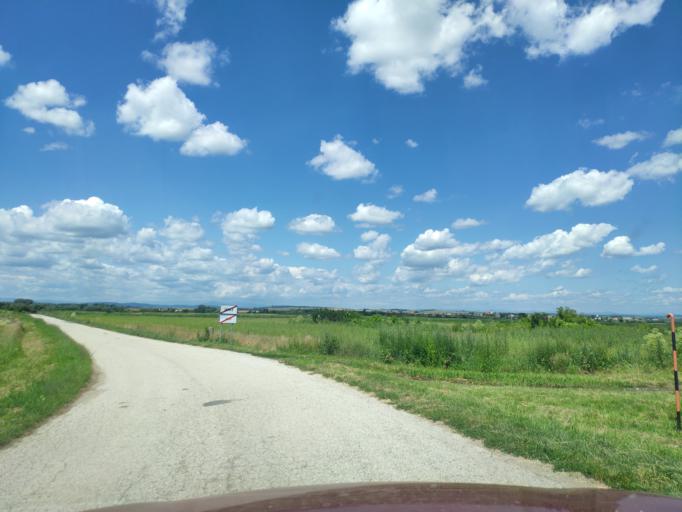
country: HU
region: Borsod-Abauj-Zemplen
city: Ozd
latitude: 48.2824
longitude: 20.2165
